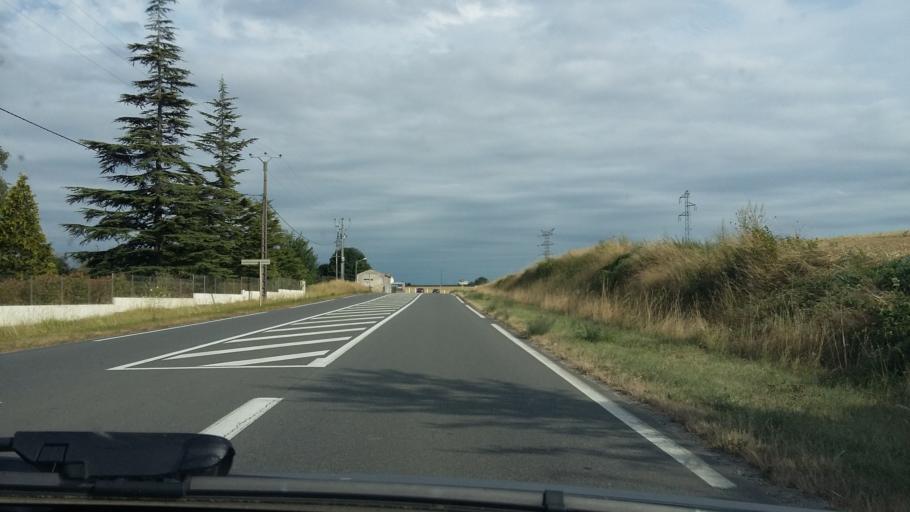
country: FR
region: Poitou-Charentes
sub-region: Departement de la Charente
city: Balzac
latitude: 45.7036
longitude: 0.0920
